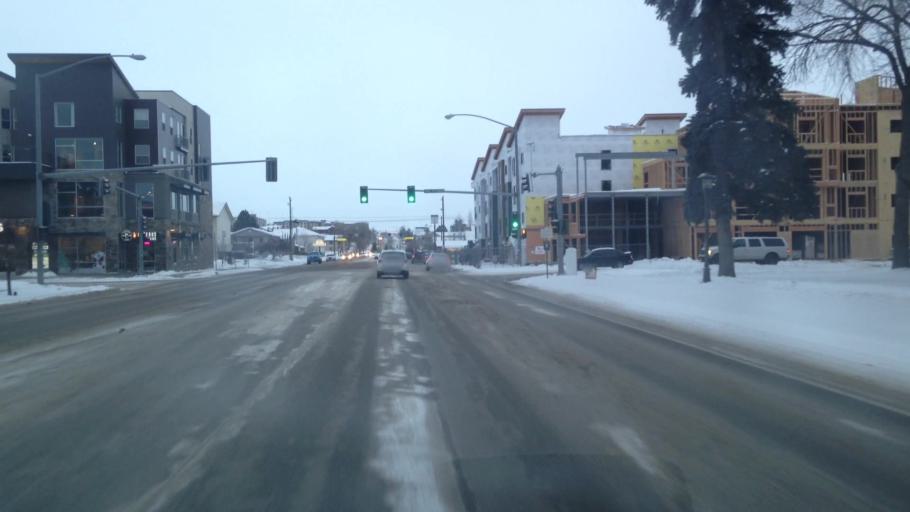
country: US
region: Idaho
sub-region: Madison County
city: Rexburg
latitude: 43.8224
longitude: -111.7896
